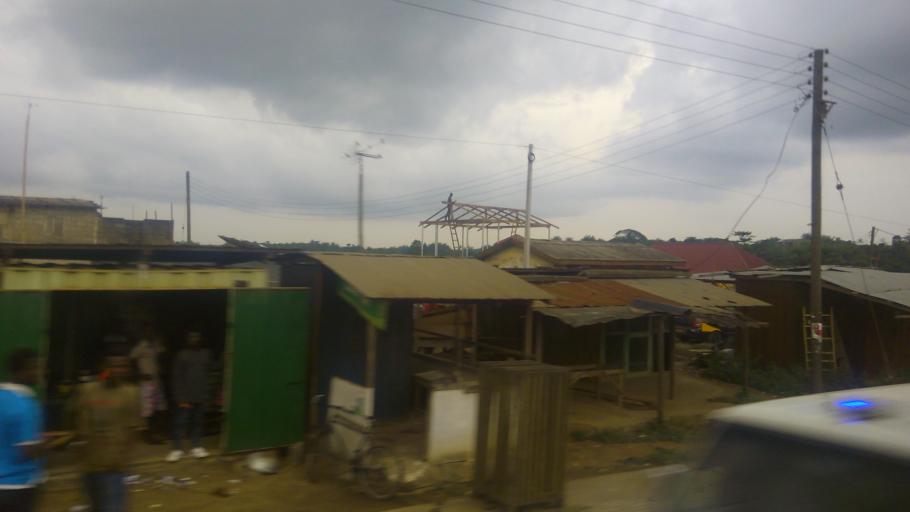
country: GH
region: Western
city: Takoradi
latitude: 4.8946
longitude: -1.9381
